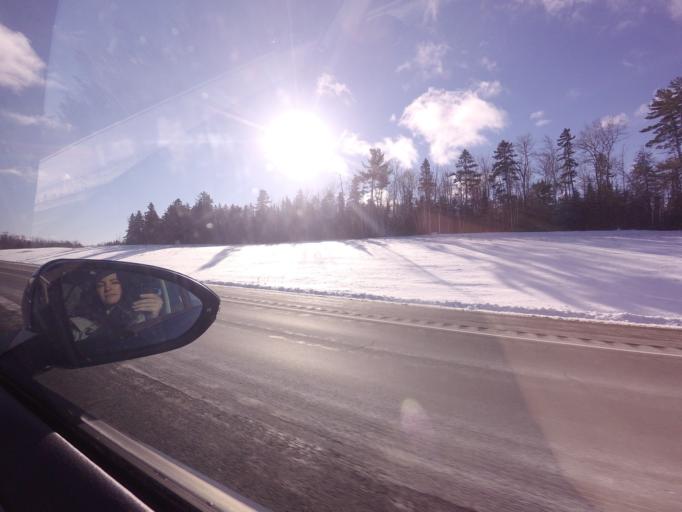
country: CA
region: New Brunswick
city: Fredericton
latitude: 45.8752
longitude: -66.6264
